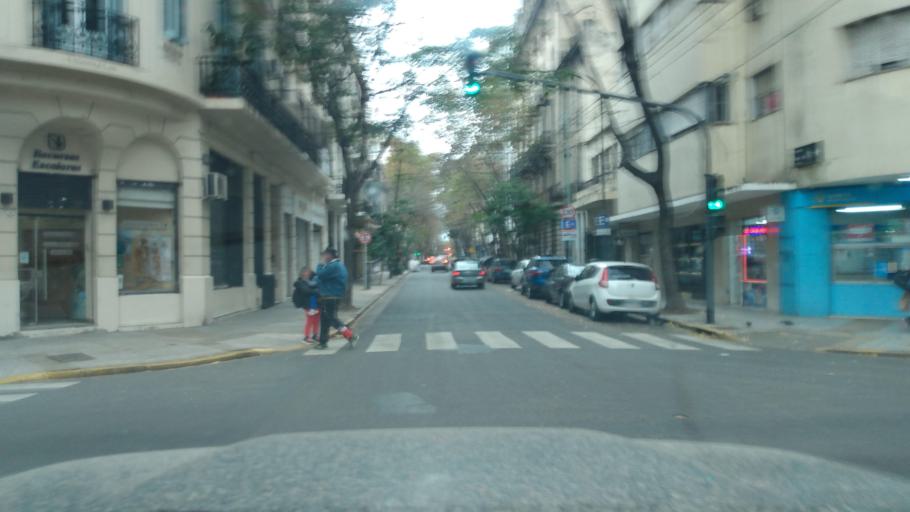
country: AR
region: Buenos Aires F.D.
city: Buenos Aires
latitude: -34.6105
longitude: -58.3963
